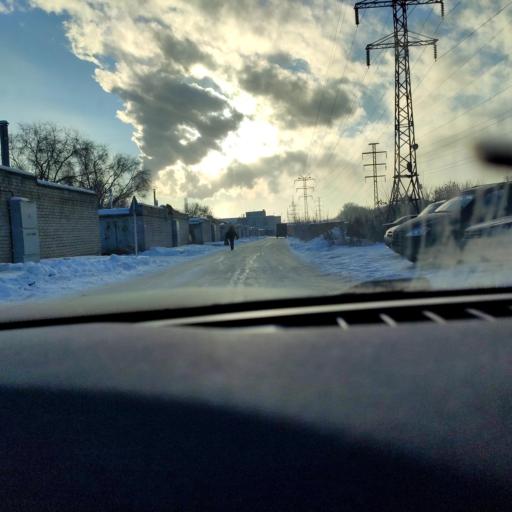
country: RU
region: Samara
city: Smyshlyayevka
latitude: 53.2090
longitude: 50.2866
